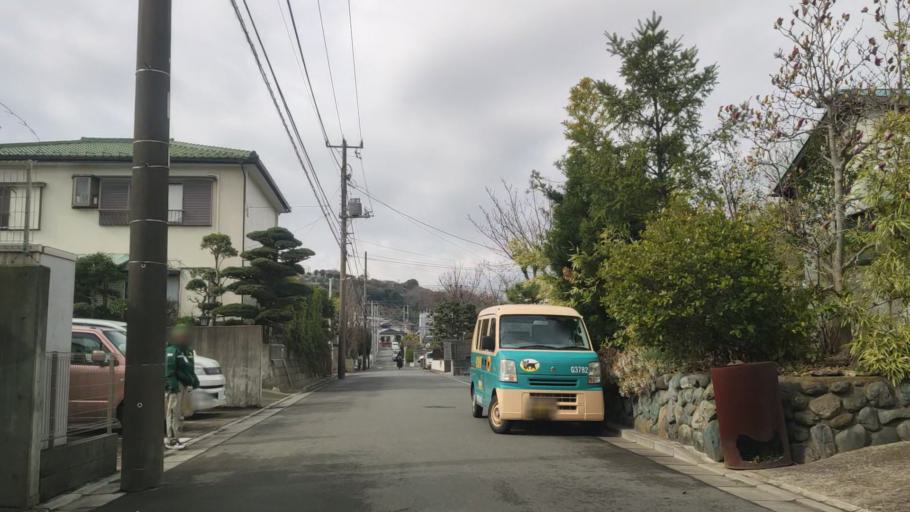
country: JP
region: Kanagawa
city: Kamakura
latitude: 35.3675
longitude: 139.5920
